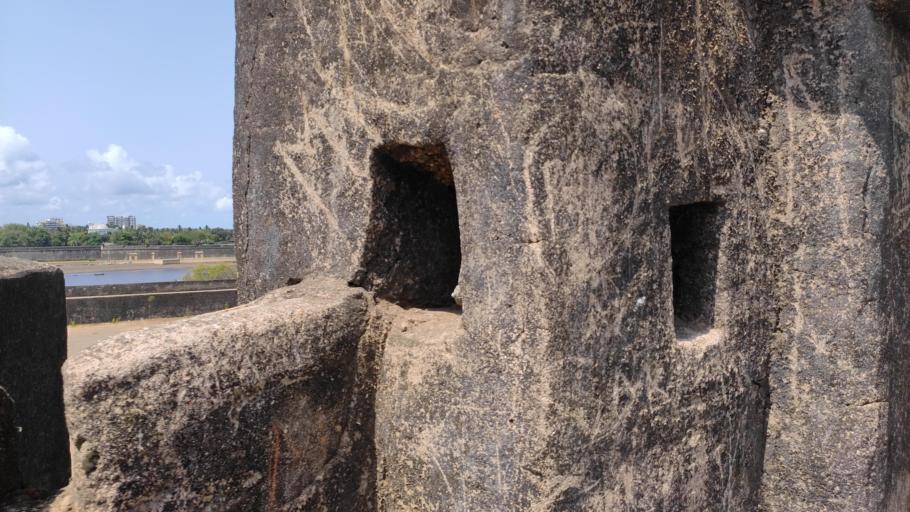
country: IN
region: Daman and Diu
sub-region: Daman District
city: Daman
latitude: 20.4139
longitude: 72.8322
